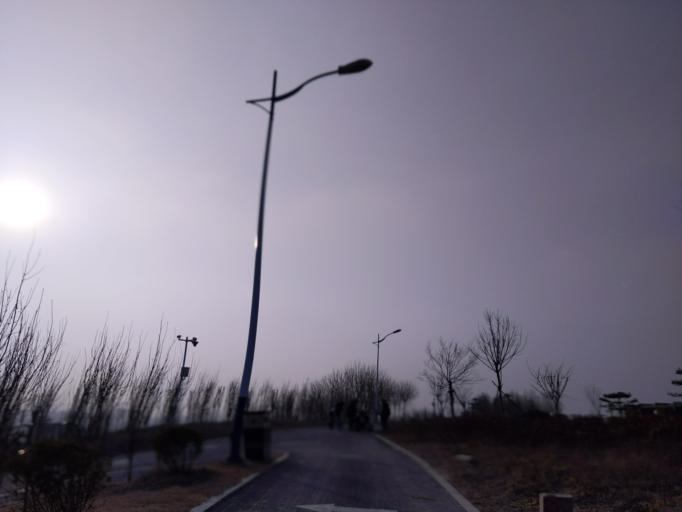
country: CN
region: Henan Sheng
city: Puyang
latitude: 35.8198
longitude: 115.0068
